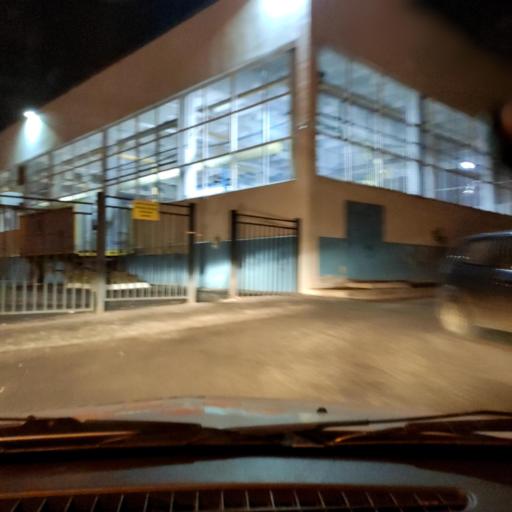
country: RU
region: Bashkortostan
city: Ufa
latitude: 54.7130
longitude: 55.9714
